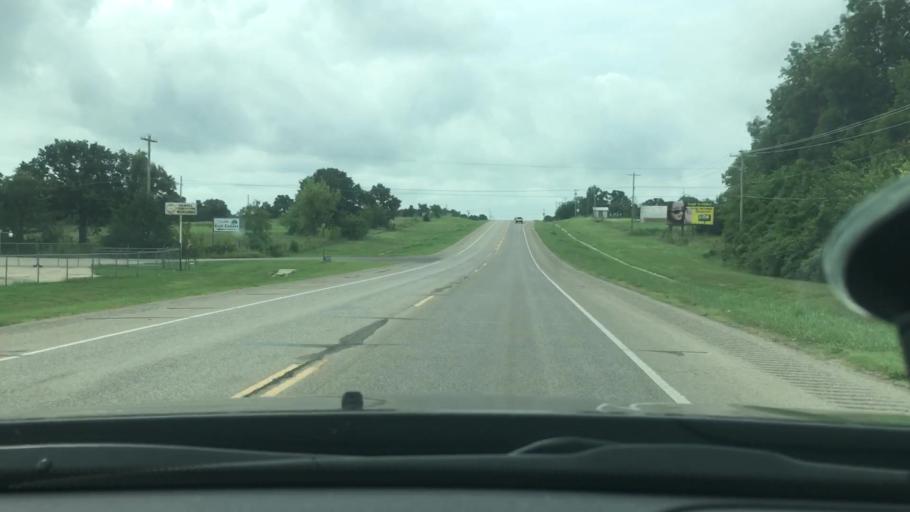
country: US
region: Oklahoma
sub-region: Carter County
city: Healdton
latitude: 34.2063
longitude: -97.4748
